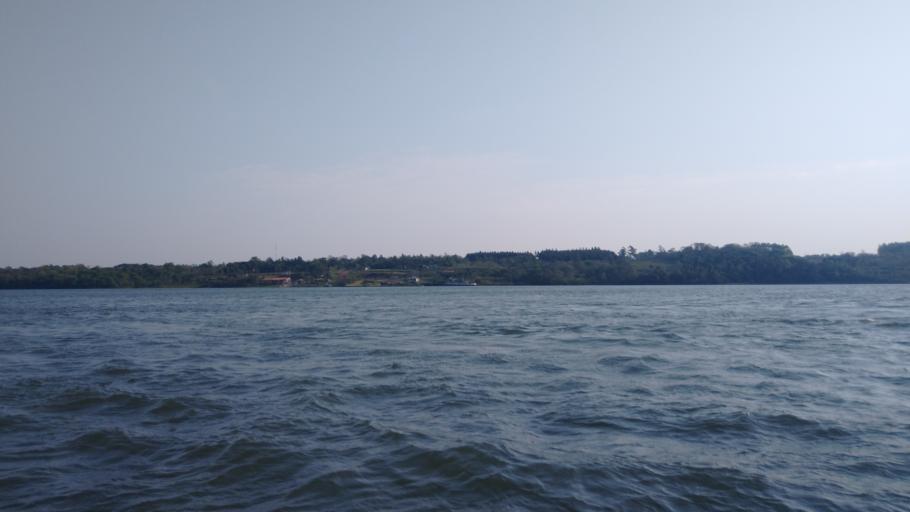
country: AR
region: Misiones
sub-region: Departamento de Candelaria
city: Candelaria
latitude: -27.4468
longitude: -55.7538
